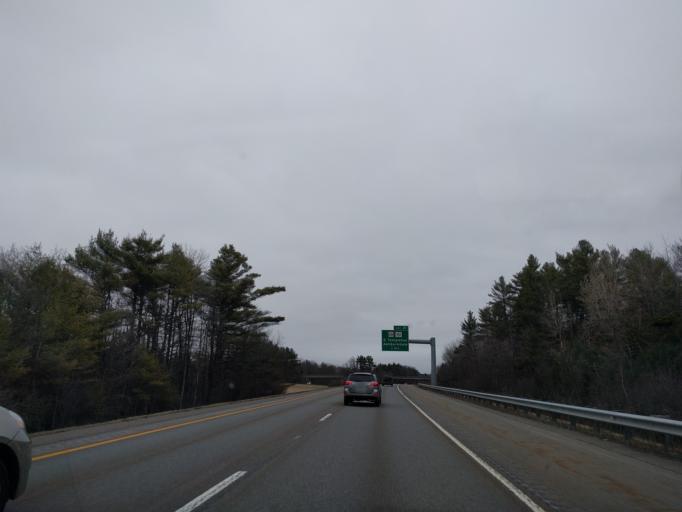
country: US
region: Massachusetts
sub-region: Worcester County
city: Templeton
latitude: 42.5668
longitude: -72.0628
